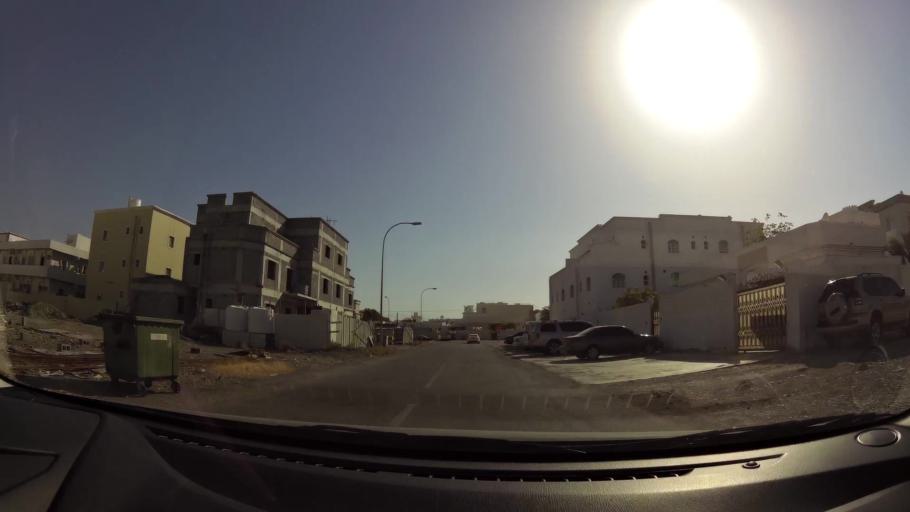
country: OM
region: Muhafazat Masqat
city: As Sib al Jadidah
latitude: 23.6197
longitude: 58.2075
